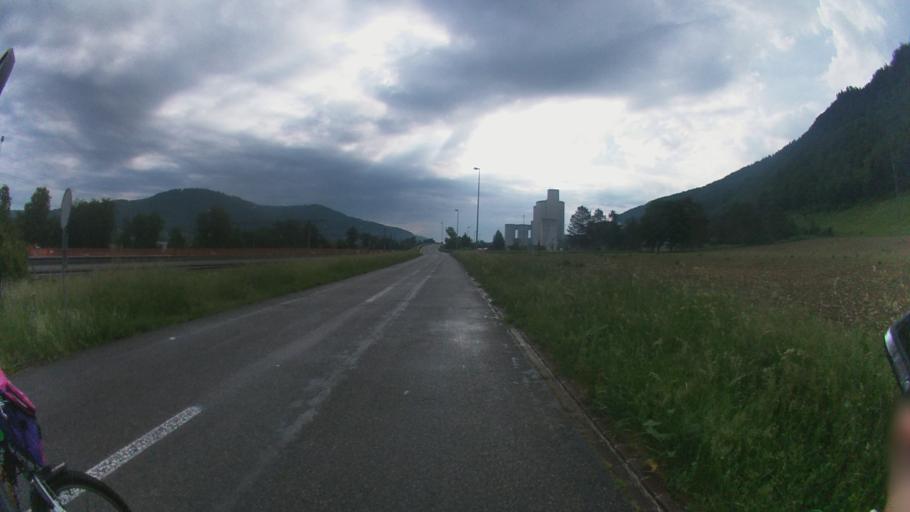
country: CH
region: Aargau
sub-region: Bezirk Zurzach
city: Bad Zurzach
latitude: 47.5730
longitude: 8.3205
